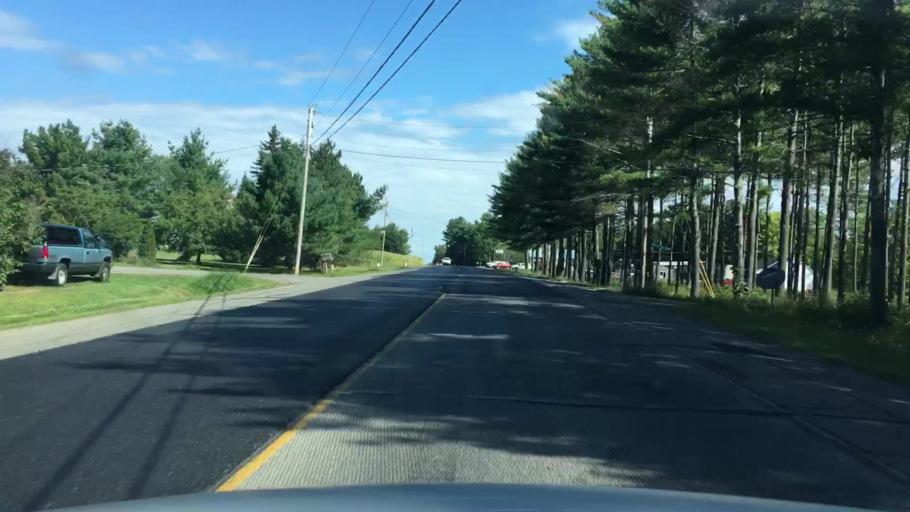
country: US
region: Maine
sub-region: Penobscot County
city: Corinna
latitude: 44.9014
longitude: -69.2659
